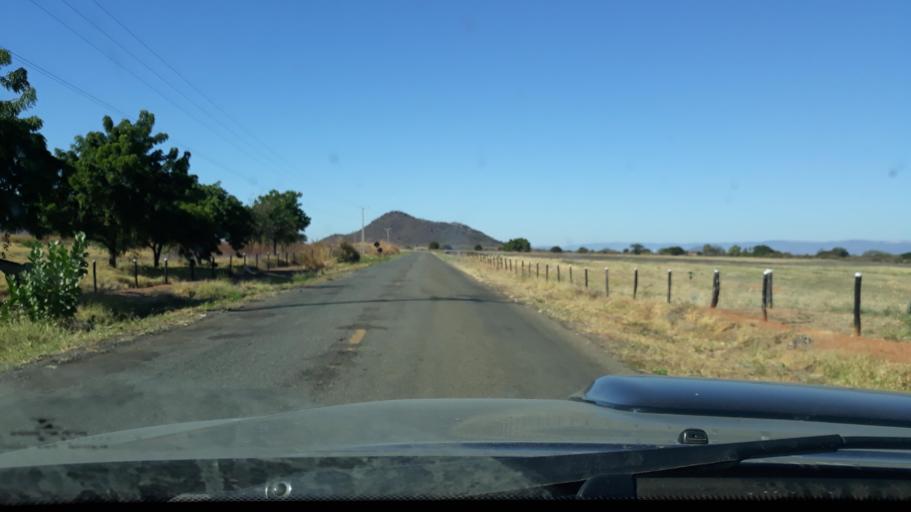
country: BR
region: Bahia
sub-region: Guanambi
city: Guanambi
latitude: -14.0974
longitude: -42.8715
